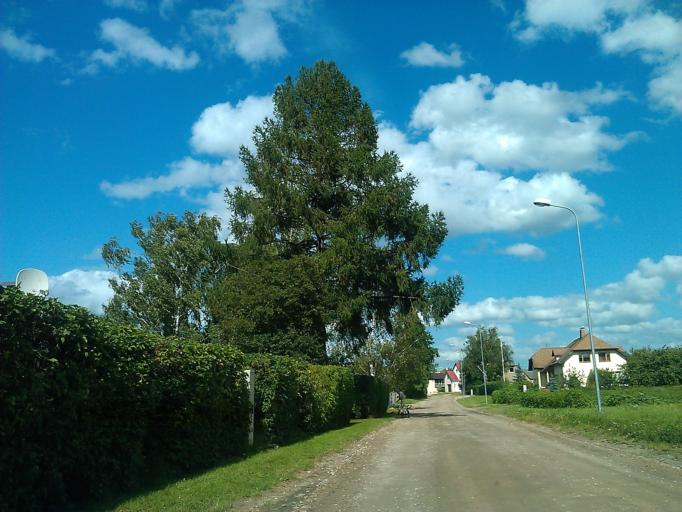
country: LV
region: Cesu Rajons
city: Cesis
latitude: 57.3040
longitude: 25.2804
